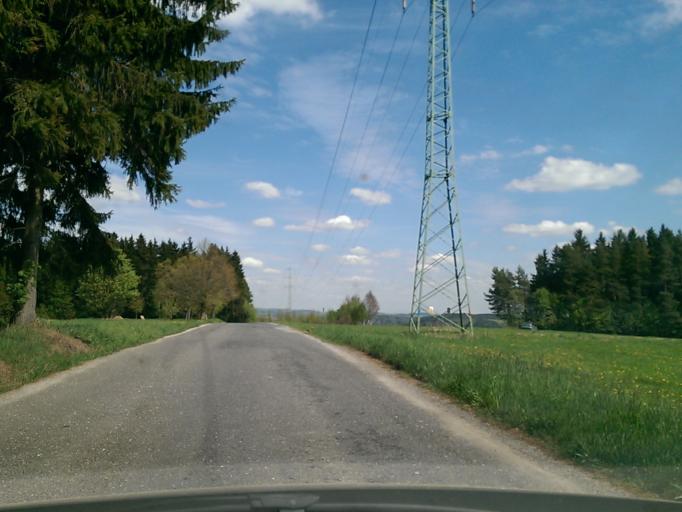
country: CZ
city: Pencin
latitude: 50.6828
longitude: 15.2202
